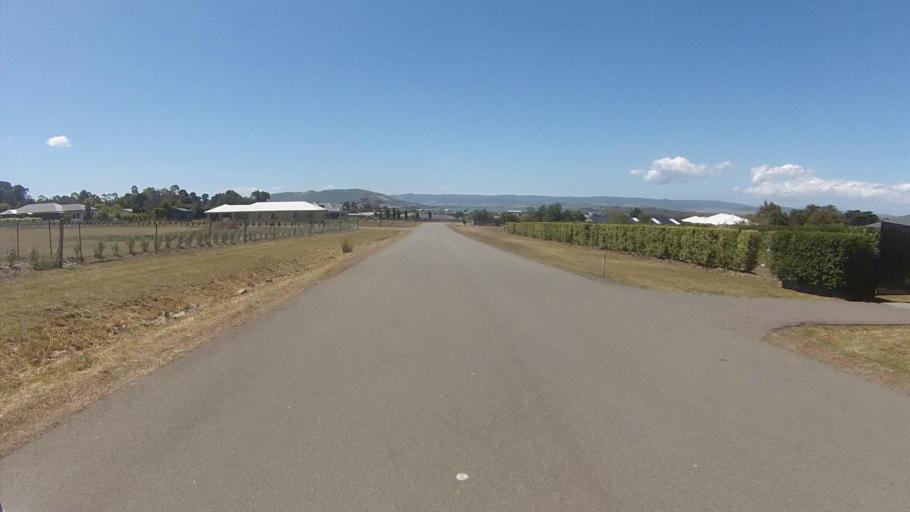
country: AU
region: Tasmania
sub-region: Clarence
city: Cambridge
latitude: -42.8454
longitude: 147.4657
